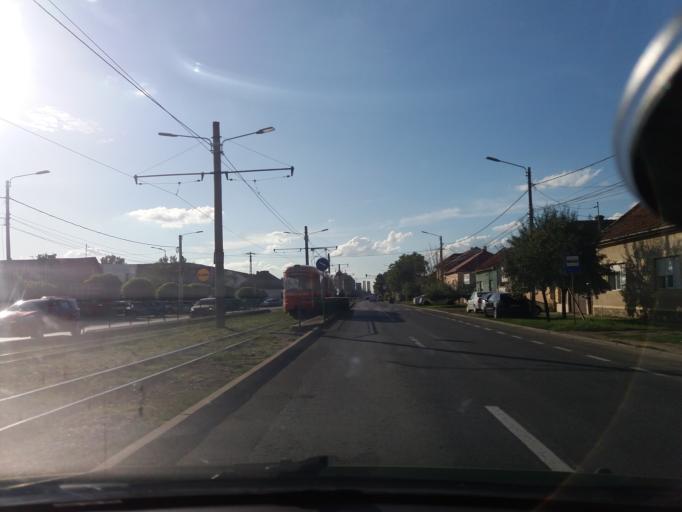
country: RO
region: Arad
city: Arad
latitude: 46.1775
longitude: 21.3566
